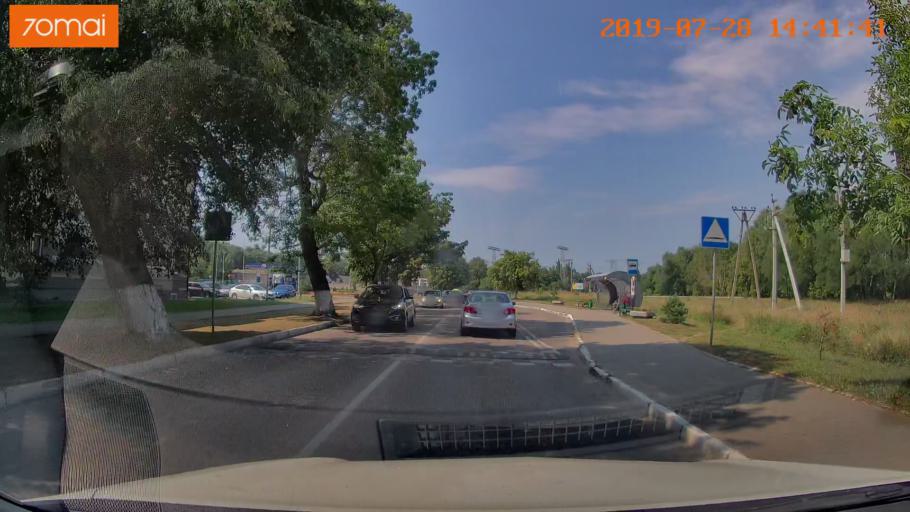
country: RU
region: Kaliningrad
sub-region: Gorod Kaliningrad
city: Yantarnyy
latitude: 54.8566
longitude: 19.9461
